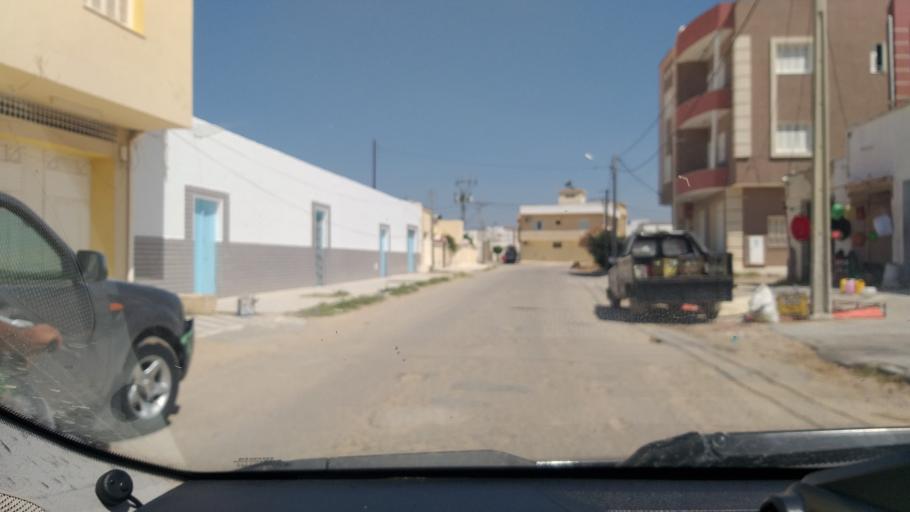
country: TN
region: Al Mahdiyah
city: El Jem
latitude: 35.2923
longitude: 10.7140
